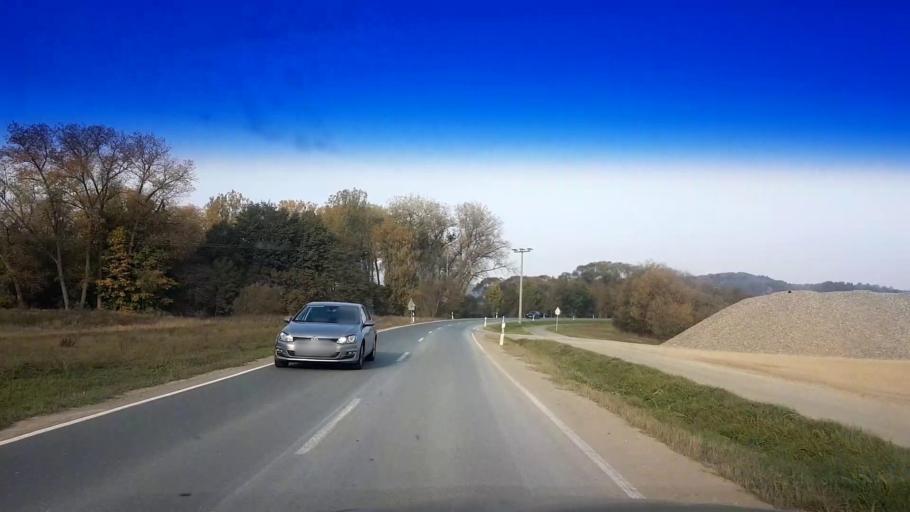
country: DE
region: Bavaria
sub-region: Upper Franconia
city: Altenkunstadt
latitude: 50.1187
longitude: 11.3025
